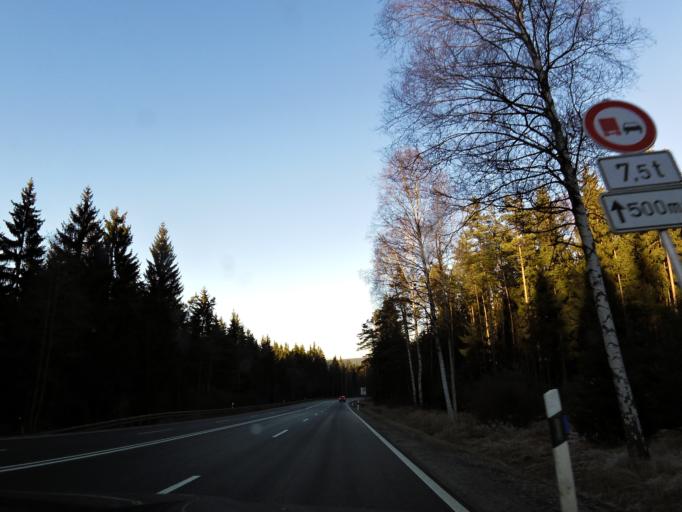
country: DE
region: Bavaria
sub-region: Upper Franconia
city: Trostau
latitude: 50.0104
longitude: 11.9259
